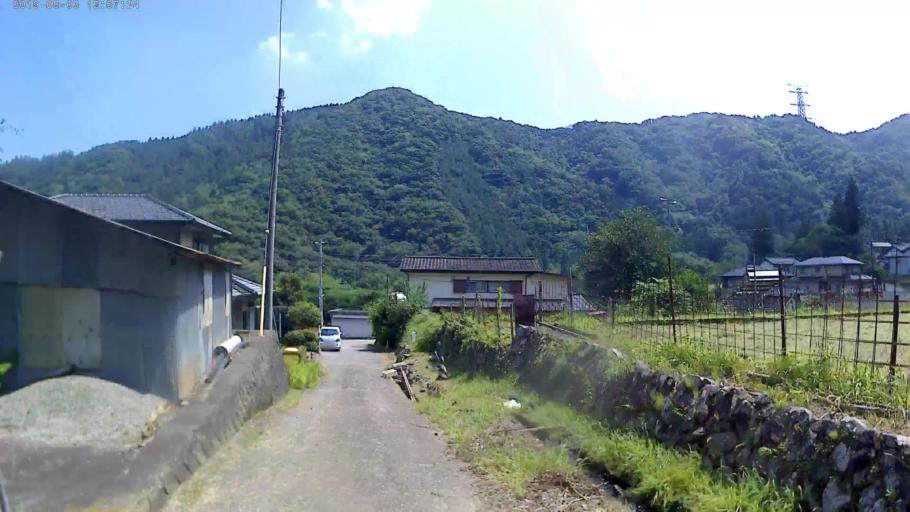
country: JP
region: Yamanashi
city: Enzan
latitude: 35.6026
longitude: 138.8013
